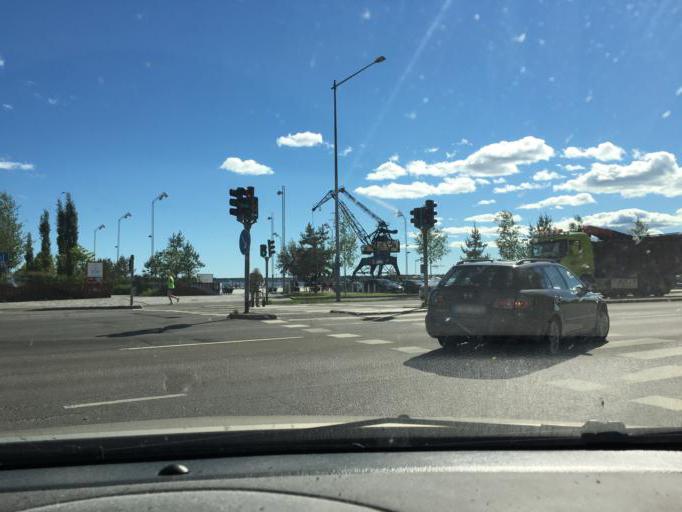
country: SE
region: Norrbotten
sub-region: Lulea Kommun
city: Lulea
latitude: 65.5814
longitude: 22.1539
